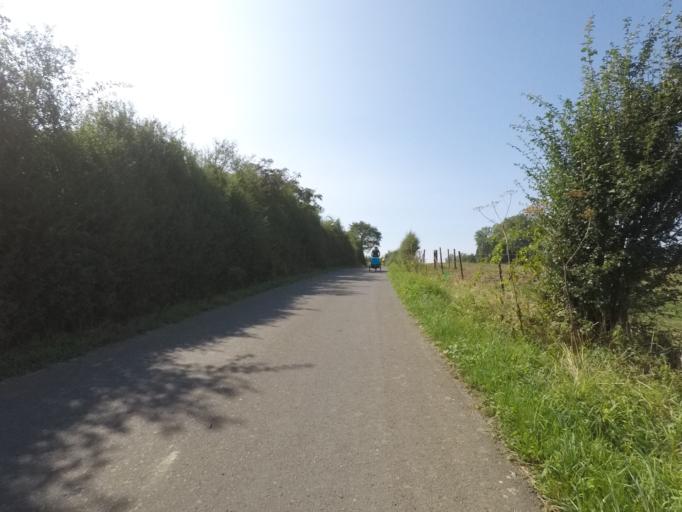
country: LU
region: Luxembourg
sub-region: Canton de Capellen
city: Mamer
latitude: 49.6444
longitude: 6.0195
